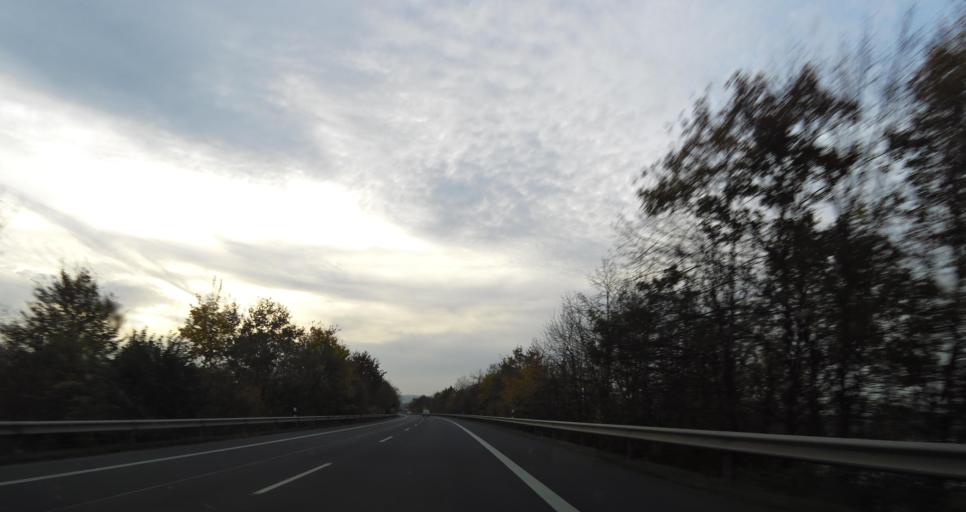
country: DE
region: Lower Saxony
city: Heyen
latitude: 51.9864
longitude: 9.4980
